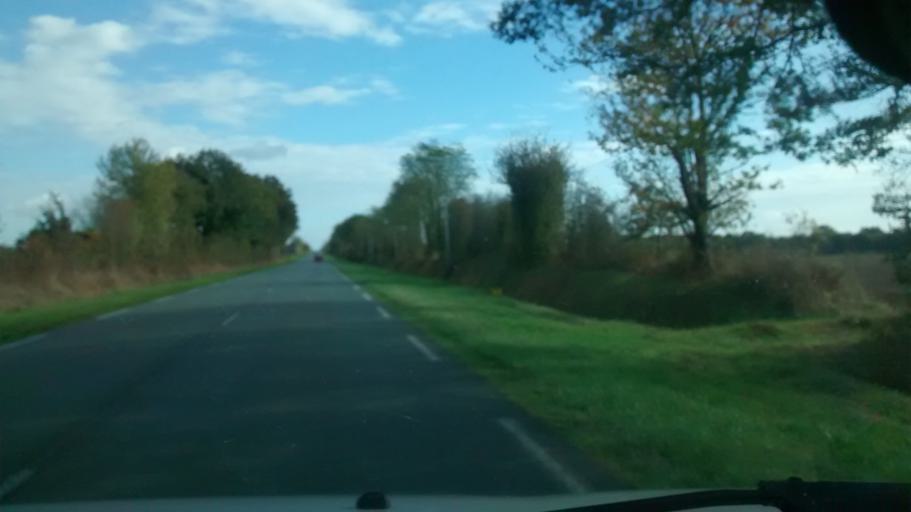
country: FR
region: Pays de la Loire
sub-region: Departement de Maine-et-Loire
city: Pouance
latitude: 47.7443
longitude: -1.2197
